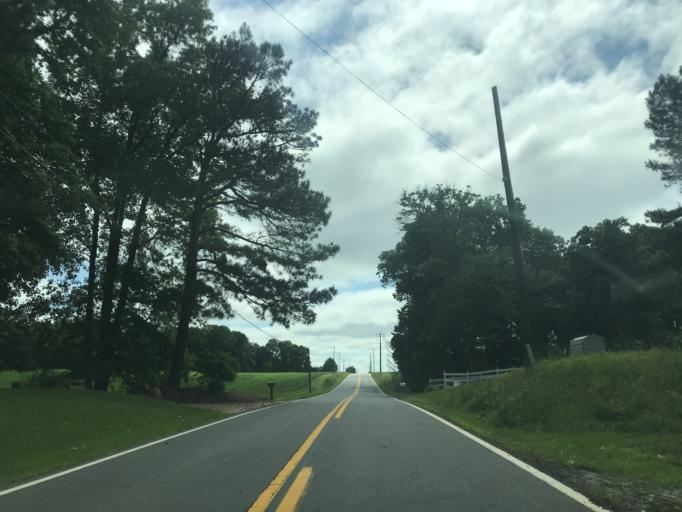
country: US
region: Maryland
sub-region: Caroline County
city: Ridgely
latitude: 38.8854
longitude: -75.9682
